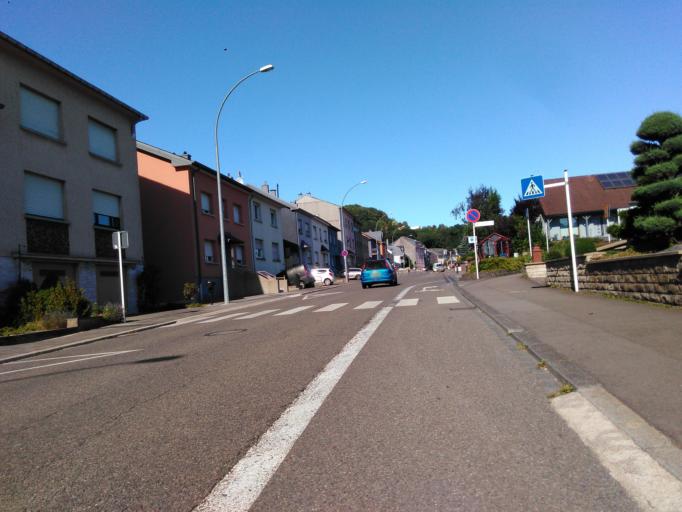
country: LU
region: Luxembourg
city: Belvaux
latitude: 49.5235
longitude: 5.9258
